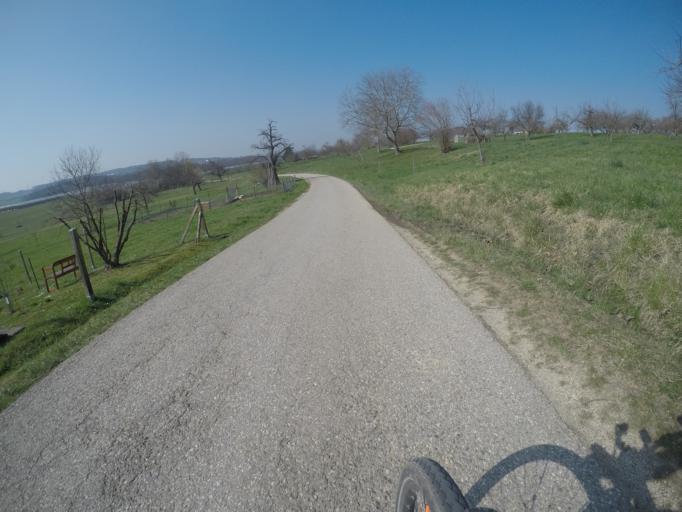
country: DE
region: Baden-Wuerttemberg
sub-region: Regierungsbezirk Stuttgart
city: Grossbettlingen
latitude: 48.6035
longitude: 9.2966
